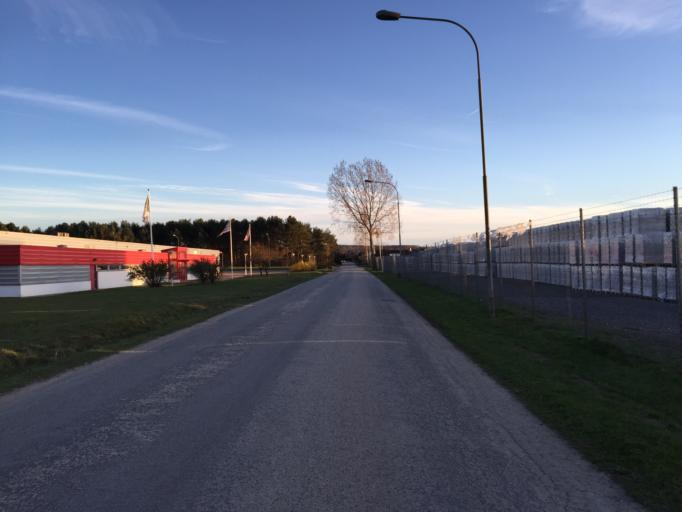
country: SE
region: Skane
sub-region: Lunds Kommun
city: Veberod
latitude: 55.6421
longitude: 13.4962
